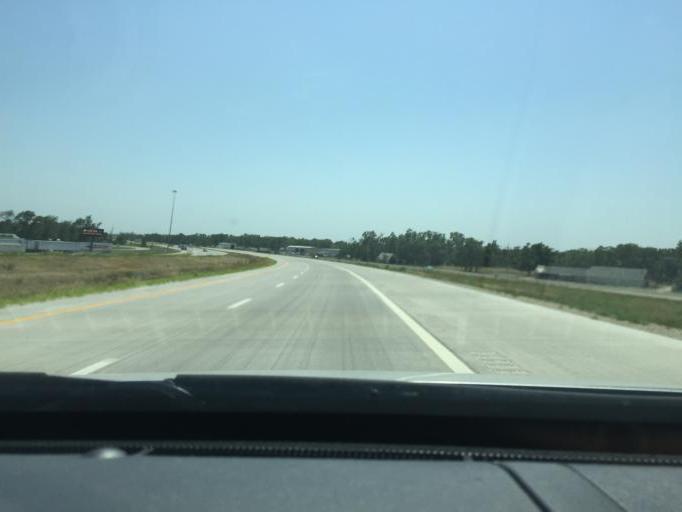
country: US
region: Kansas
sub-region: Reno County
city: South Hutchinson
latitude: 38.0273
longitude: -97.9050
